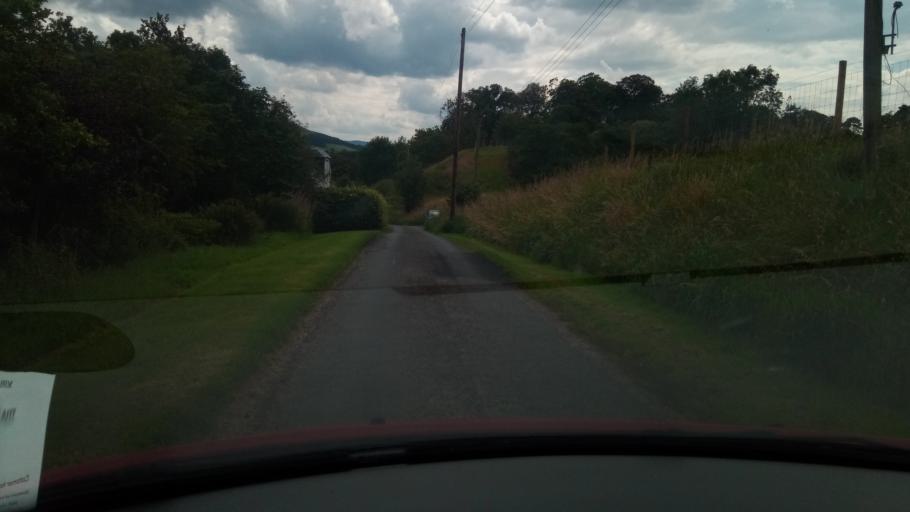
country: GB
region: Scotland
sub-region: The Scottish Borders
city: Jedburgh
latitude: 55.4300
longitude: -2.6361
